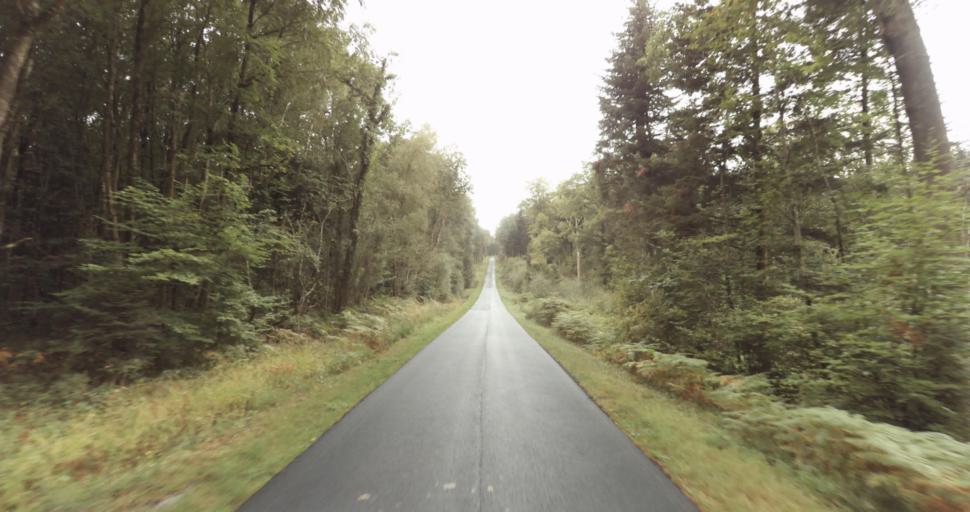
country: FR
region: Lower Normandy
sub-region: Departement de l'Orne
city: Sainte-Gauburge-Sainte-Colombe
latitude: 48.7553
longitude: 0.4829
